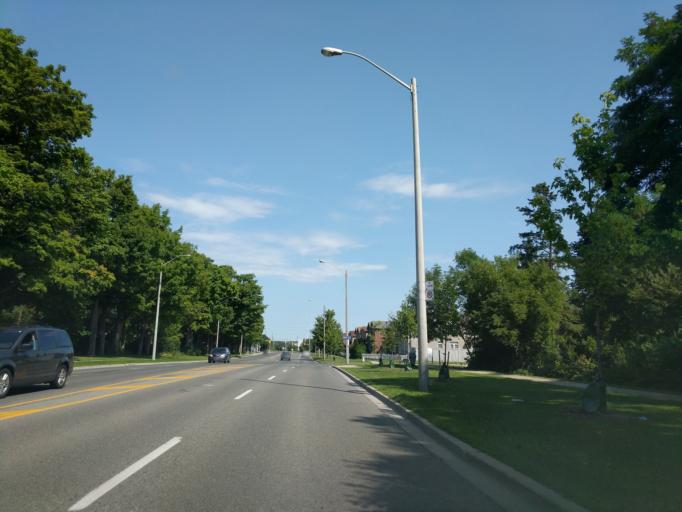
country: CA
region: Ontario
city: Scarborough
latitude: 43.8139
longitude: -79.2264
